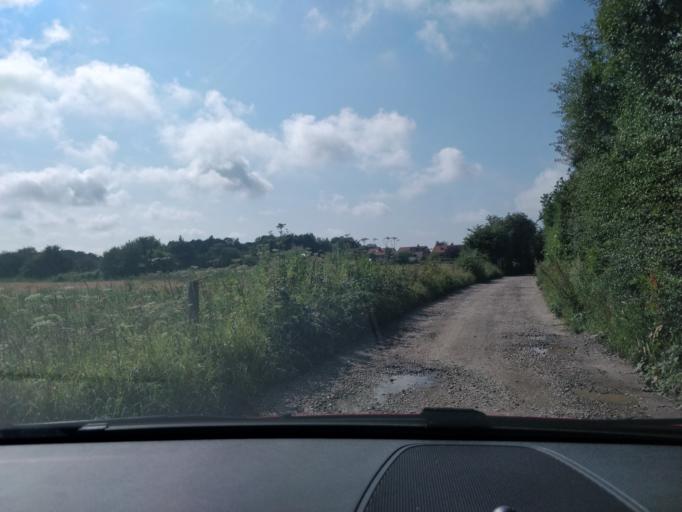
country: GB
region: England
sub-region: Lancashire
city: Banks
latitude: 53.6630
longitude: -2.9507
